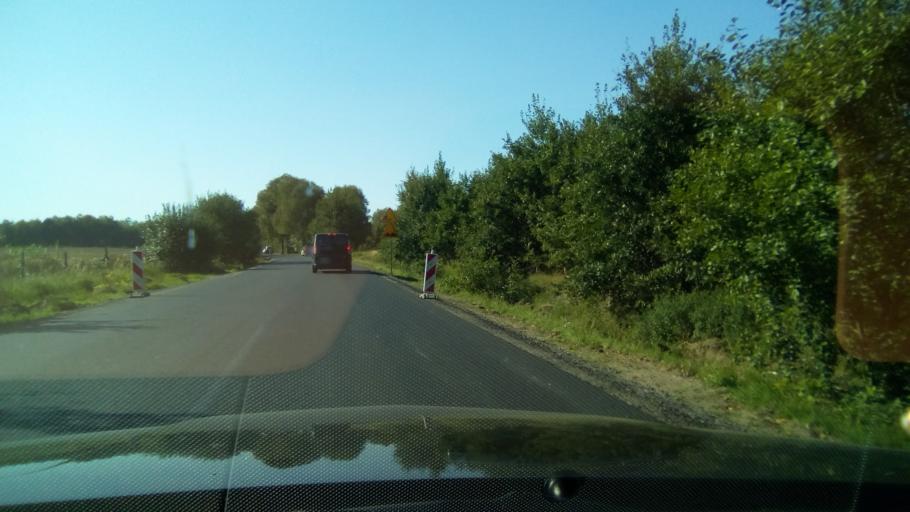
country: PL
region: West Pomeranian Voivodeship
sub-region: Powiat gryficki
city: Ploty
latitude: 53.8123
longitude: 15.1932
